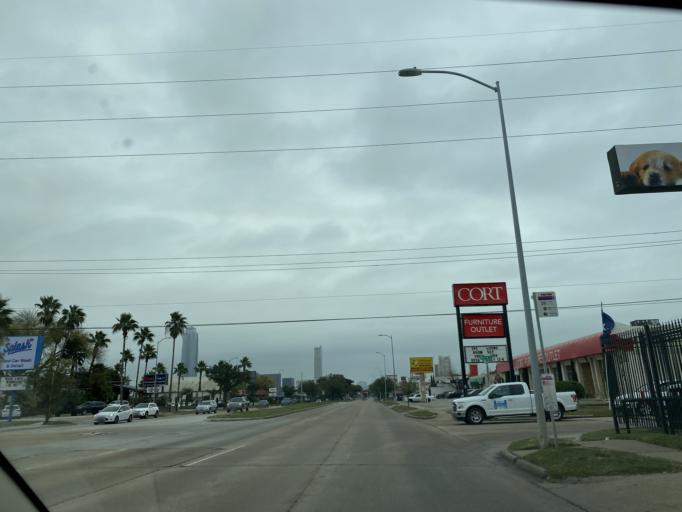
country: US
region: Texas
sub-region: Harris County
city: Bellaire
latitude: 29.7314
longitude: -95.4807
